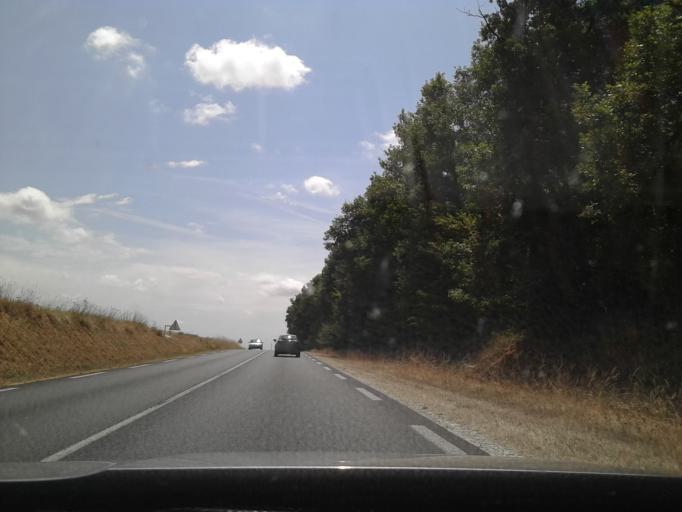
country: FR
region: Centre
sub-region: Departement d'Indre-et-Loire
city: Poce-sur-Cisse
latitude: 47.4983
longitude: 1.0047
